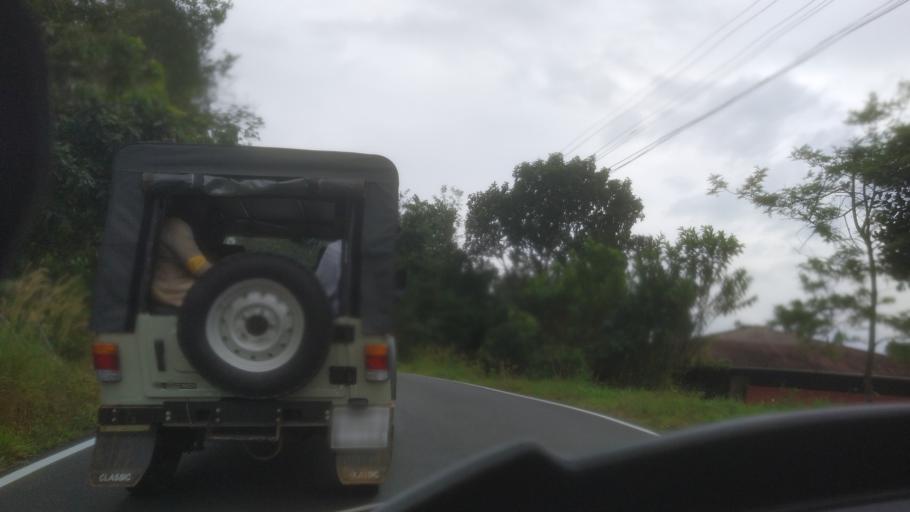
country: IN
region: Kerala
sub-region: Idukki
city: Idukki
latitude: 9.9407
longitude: 77.0256
